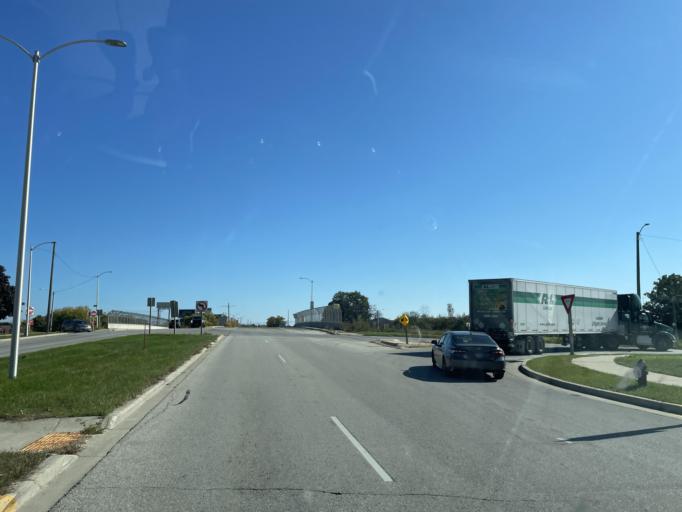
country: US
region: Wisconsin
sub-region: Waukesha County
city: Butler
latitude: 43.1202
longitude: -88.0360
